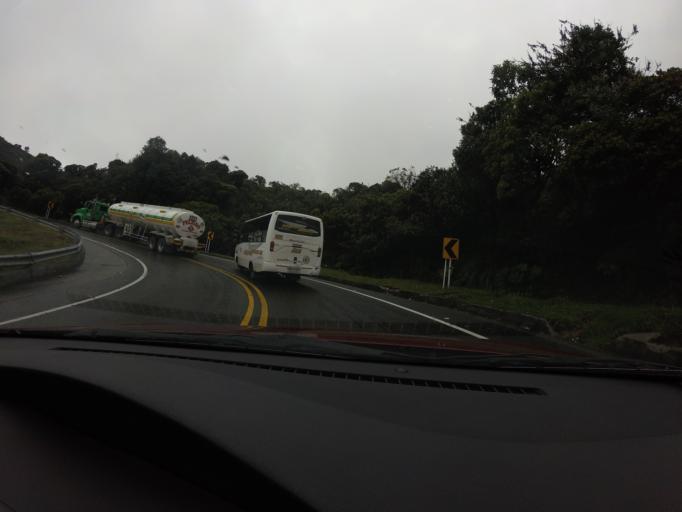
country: CO
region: Tolima
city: Herveo
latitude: 5.0755
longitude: -75.2836
